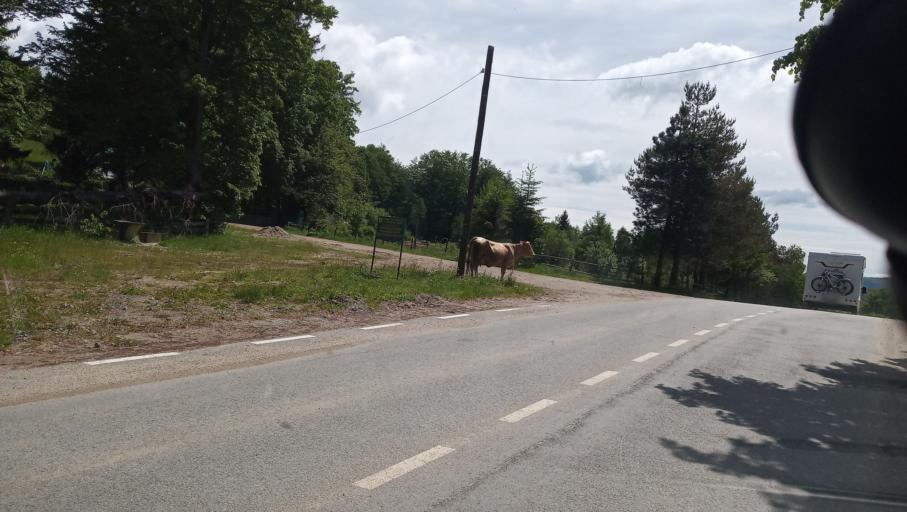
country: RO
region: Caras-Severin
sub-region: Comuna Valiug
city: Valiug
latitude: 45.2248
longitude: 22.0748
